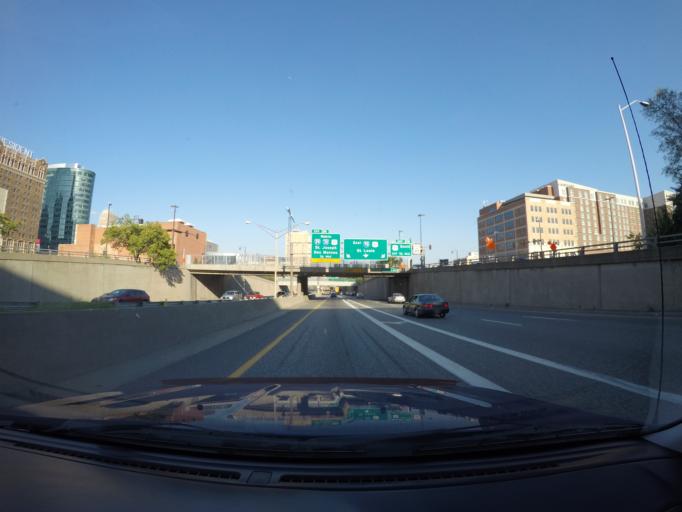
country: US
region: Missouri
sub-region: Jackson County
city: Kansas City
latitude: 39.0962
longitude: -94.5856
